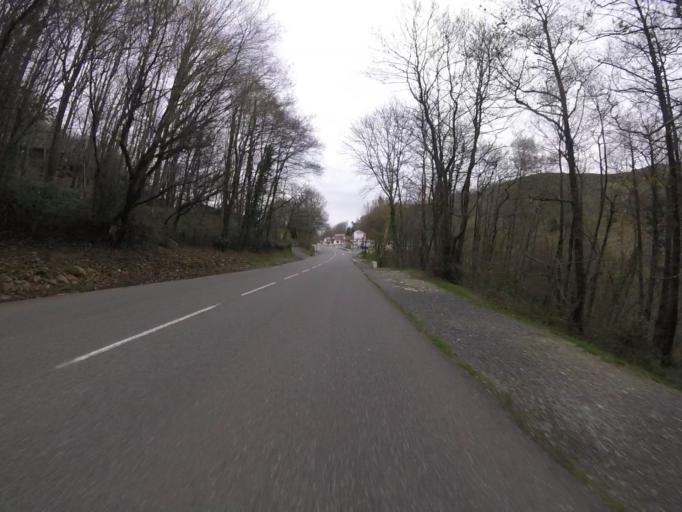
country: FR
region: Aquitaine
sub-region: Departement des Pyrenees-Atlantiques
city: Sare
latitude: 43.3268
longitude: -1.6013
